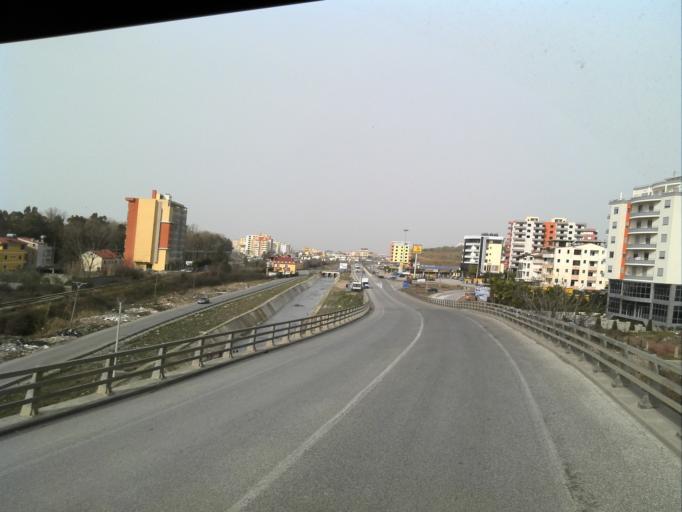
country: AL
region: Durres
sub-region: Rrethi i Durresit
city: Rrashbull
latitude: 41.2937
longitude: 19.5095
